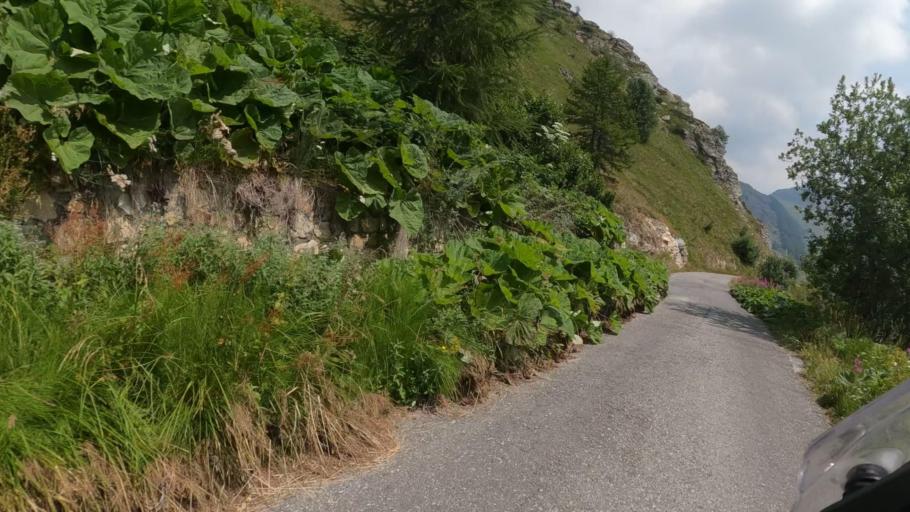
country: IT
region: Piedmont
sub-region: Provincia di Cuneo
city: Campomolino
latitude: 44.3973
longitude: 7.1604
